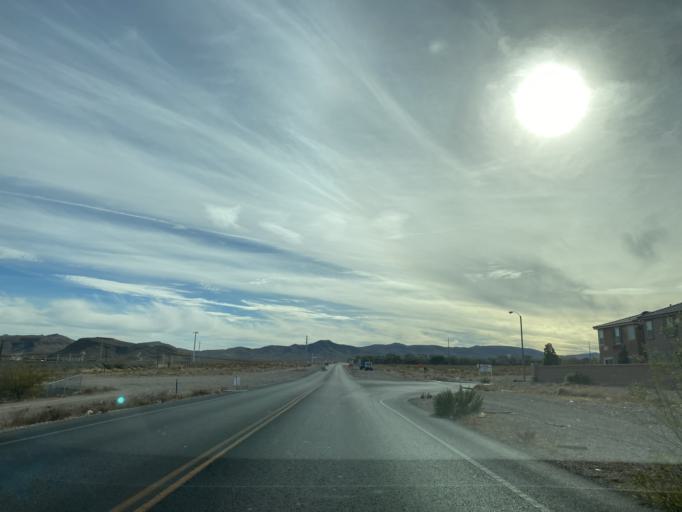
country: US
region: Nevada
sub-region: Clark County
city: Enterprise
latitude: 35.9959
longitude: -115.2435
